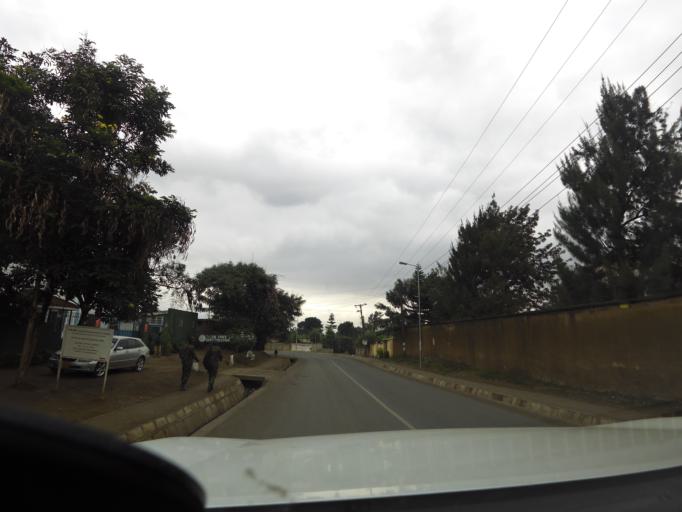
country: TZ
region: Arusha
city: Arusha
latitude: -3.3616
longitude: 36.6600
